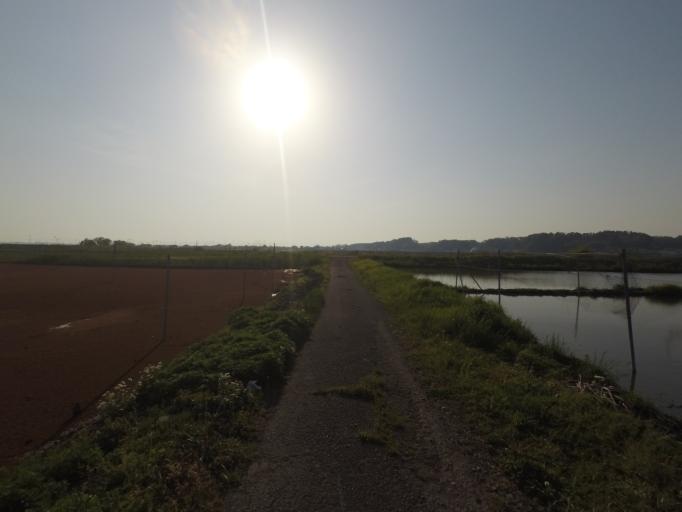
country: JP
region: Ibaraki
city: Ami
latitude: 36.0699
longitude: 140.2661
